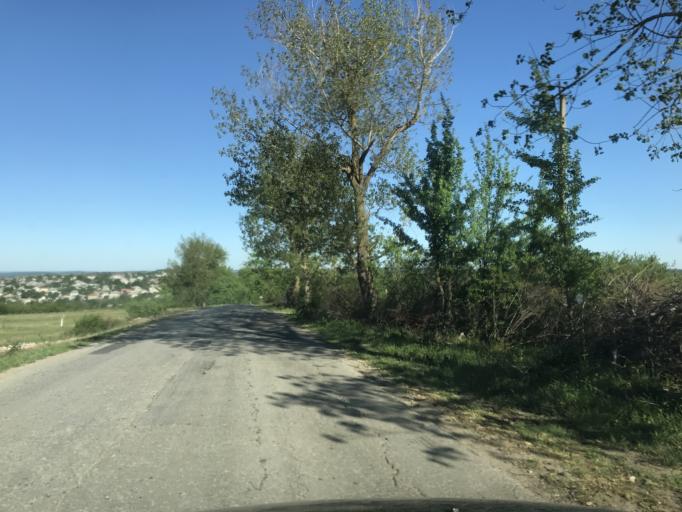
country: MD
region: Orhei
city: Orhei
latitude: 47.2622
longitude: 28.7895
